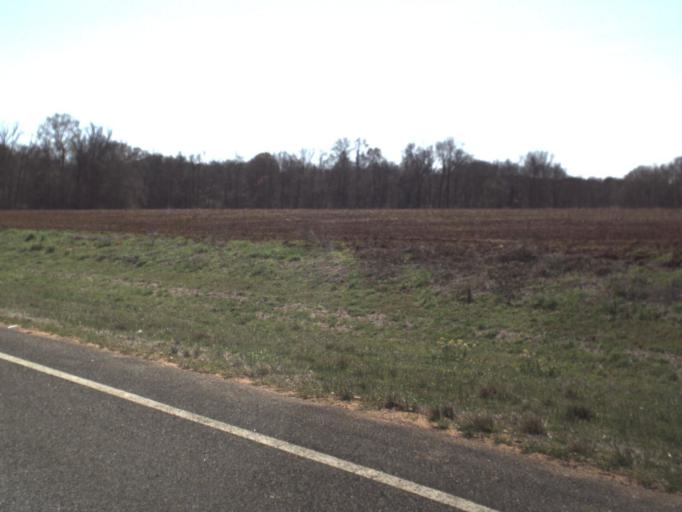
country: US
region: Florida
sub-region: Jackson County
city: Marianna
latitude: 30.8576
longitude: -85.3535
